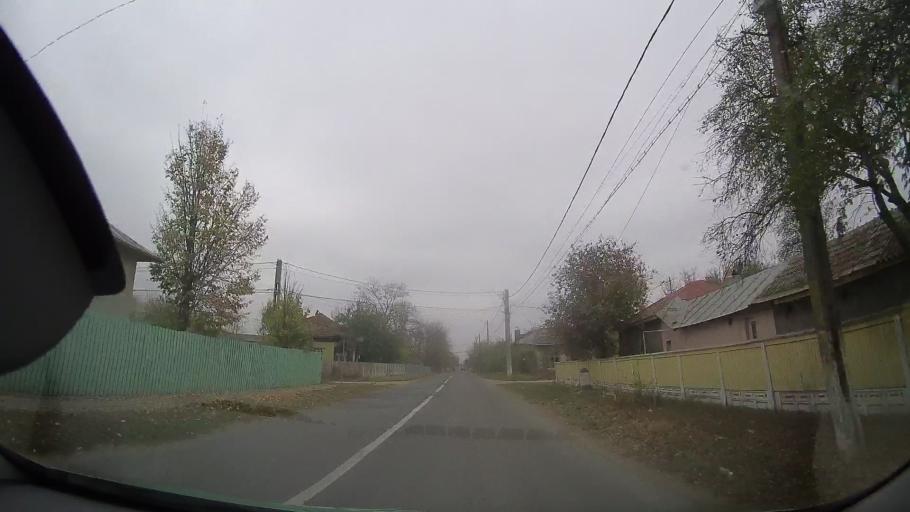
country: RO
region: Ialomita
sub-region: Comuna Grindu
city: Grindu
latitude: 44.7752
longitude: 26.9050
